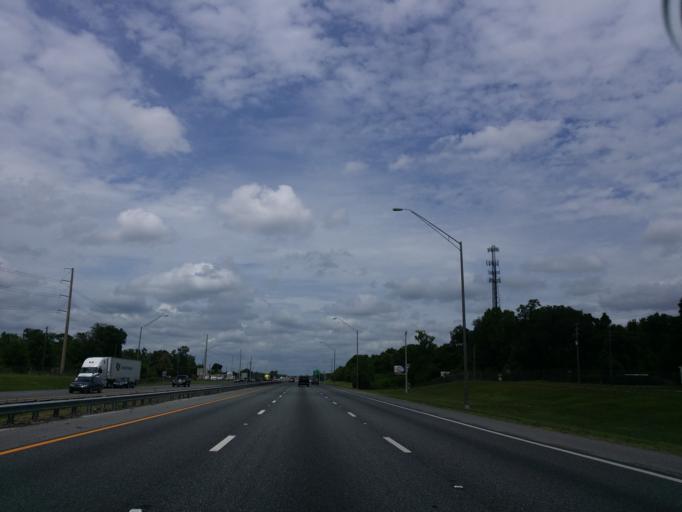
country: US
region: Florida
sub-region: Marion County
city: Ocala
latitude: 29.1961
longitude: -82.1845
